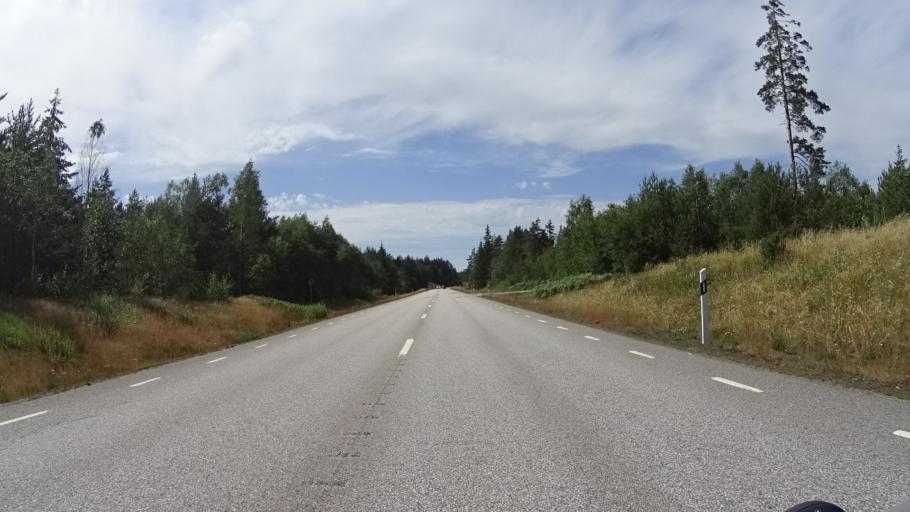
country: SE
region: Kalmar
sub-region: Vasterviks Kommun
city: Overum
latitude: 57.9625
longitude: 16.3542
